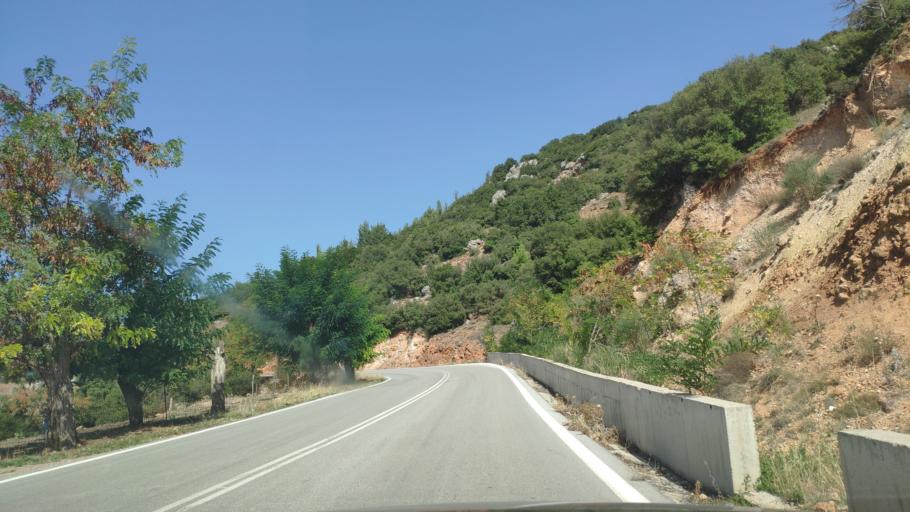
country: GR
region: West Greece
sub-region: Nomos Achaias
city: Aiyira
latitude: 37.9245
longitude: 22.3393
